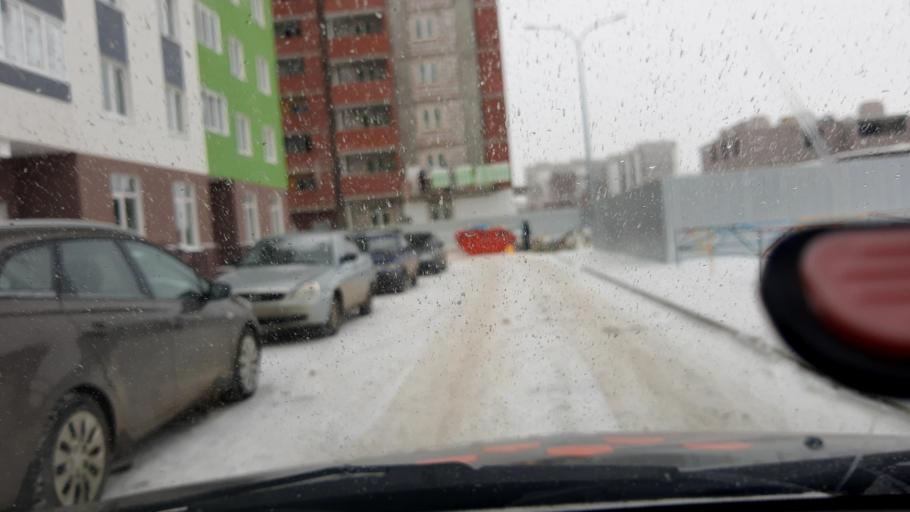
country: RU
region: Bashkortostan
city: Avdon
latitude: 54.7100
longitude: 55.8101
